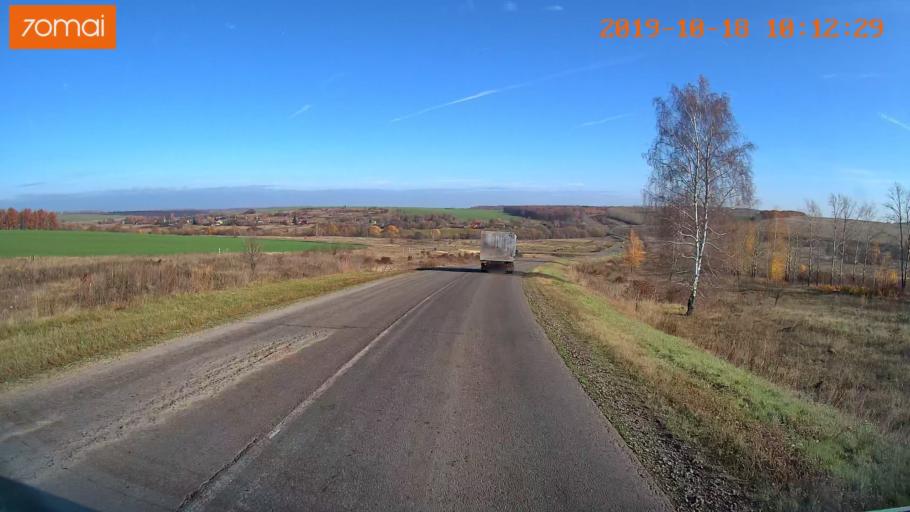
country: RU
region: Tula
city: Kurkino
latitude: 53.3944
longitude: 38.5080
